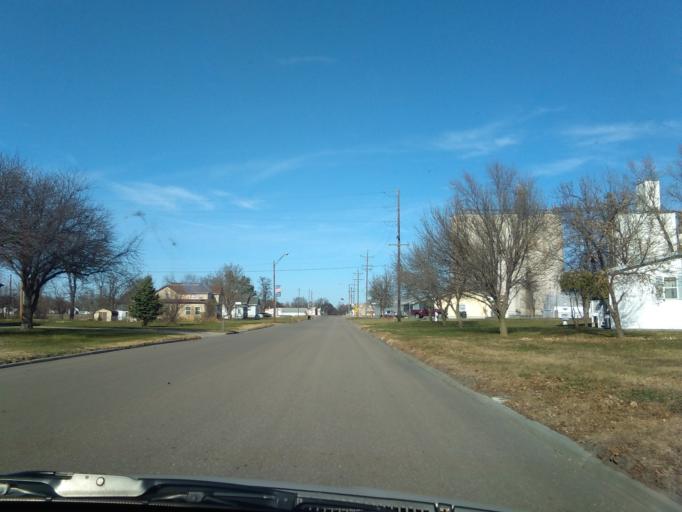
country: US
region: Nebraska
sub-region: Clay County
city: Harvard
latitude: 40.6145
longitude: -98.0972
